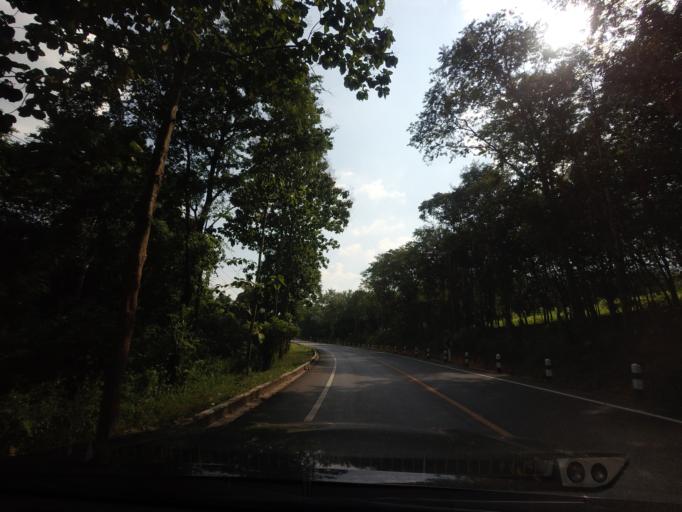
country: TH
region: Nan
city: Santi Suk
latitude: 18.9827
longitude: 100.9312
